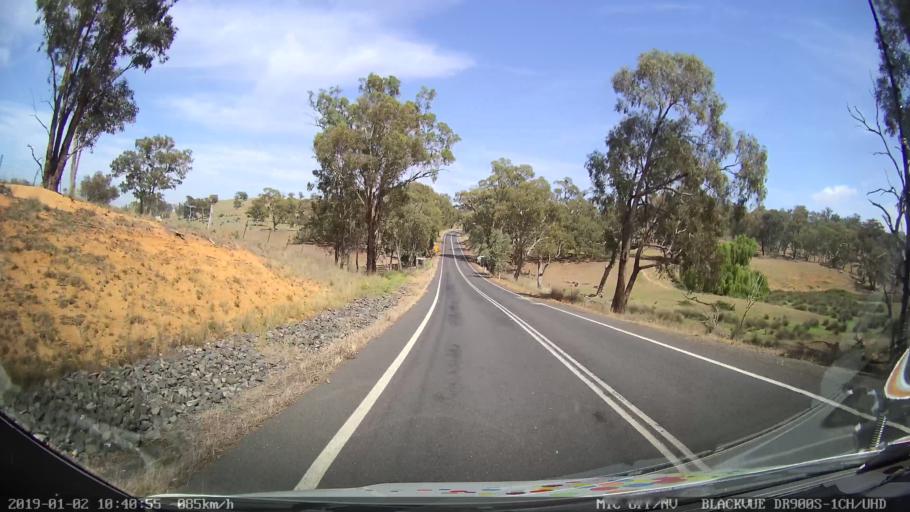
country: AU
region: New South Wales
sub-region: Cootamundra
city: Cootamundra
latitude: -34.7975
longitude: 148.3118
